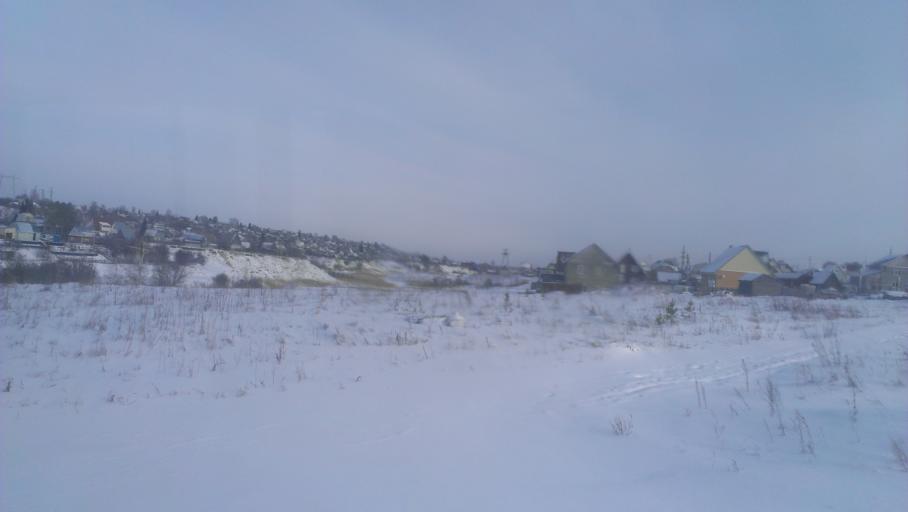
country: RU
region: Altai Krai
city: Gon'ba
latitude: 53.4143
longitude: 83.5511
